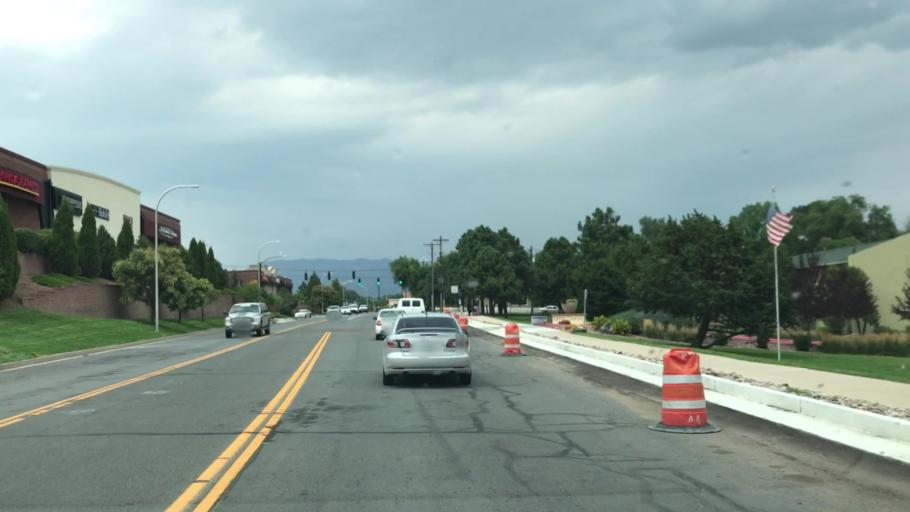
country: US
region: Colorado
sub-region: El Paso County
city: Colorado Springs
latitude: 38.8035
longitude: -104.8182
